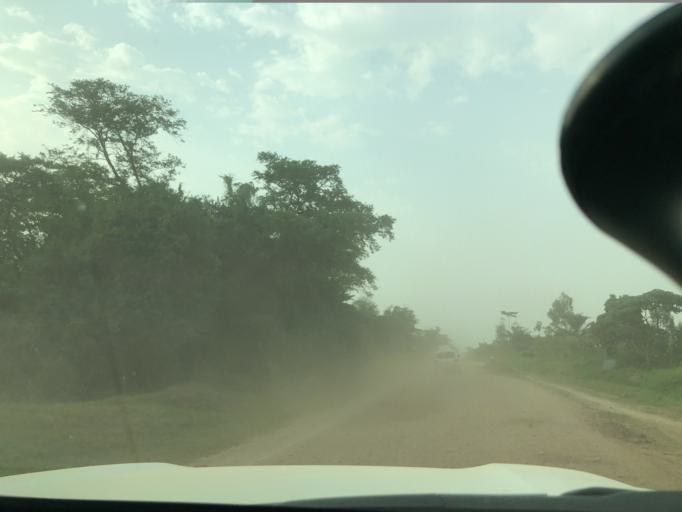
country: UG
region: Western Region
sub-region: Kasese District
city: Margherita
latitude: 0.2624
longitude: 29.6776
